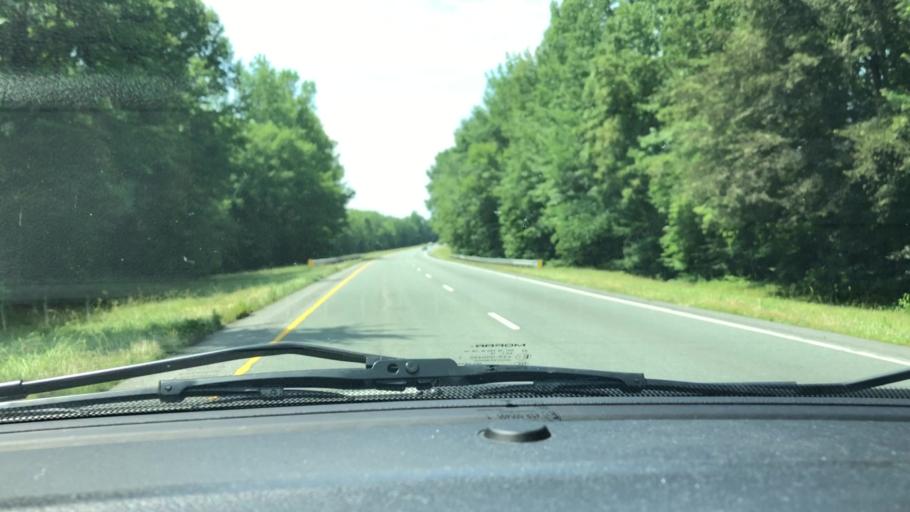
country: US
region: North Carolina
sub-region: Randolph County
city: Liberty
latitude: 35.8673
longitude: -79.6269
